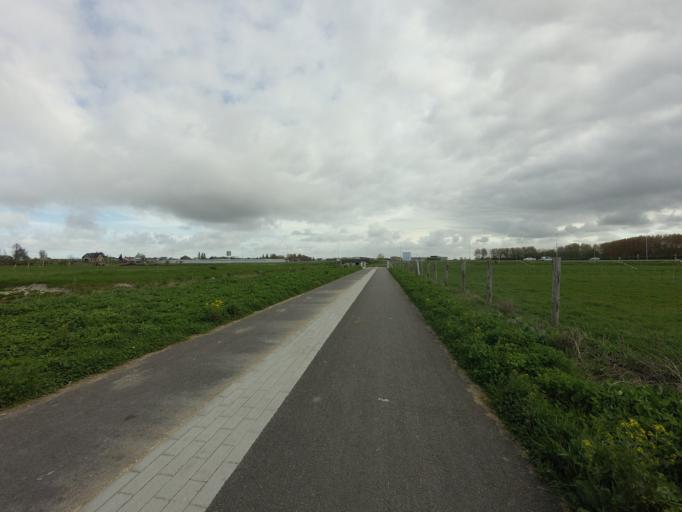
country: NL
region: South Holland
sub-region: Gemeente Lansingerland
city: Berkel en Rodenrijs
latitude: 51.9691
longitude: 4.4522
